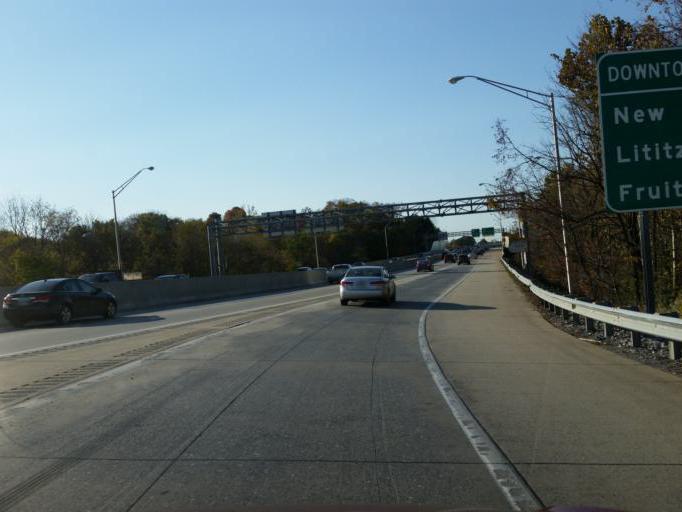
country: US
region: Pennsylvania
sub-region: Lancaster County
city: Lancaster
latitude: 40.0564
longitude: -76.2702
